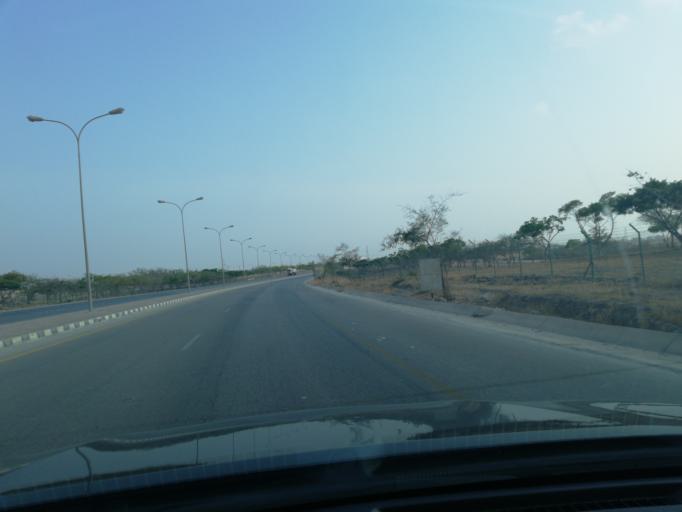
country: OM
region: Zufar
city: Salalah
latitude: 17.1145
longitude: 54.1530
